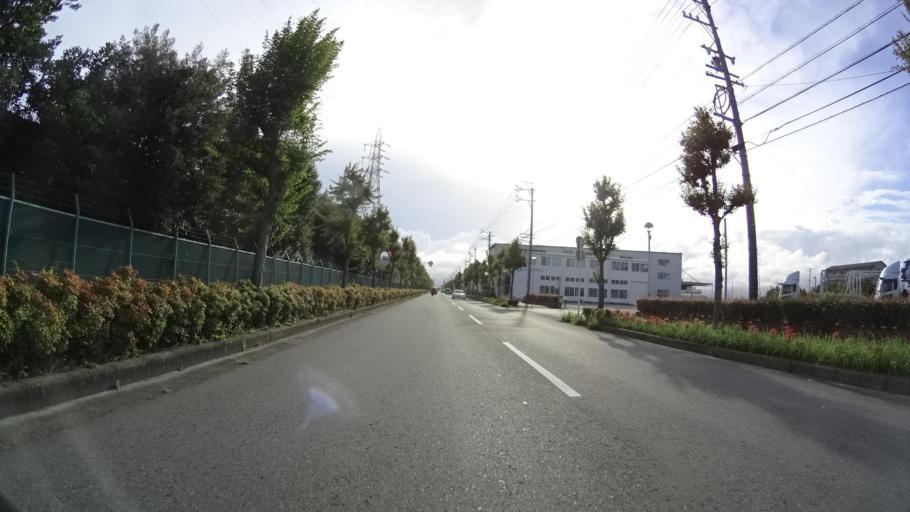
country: JP
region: Mie
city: Suzuka
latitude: 34.8681
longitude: 136.5276
